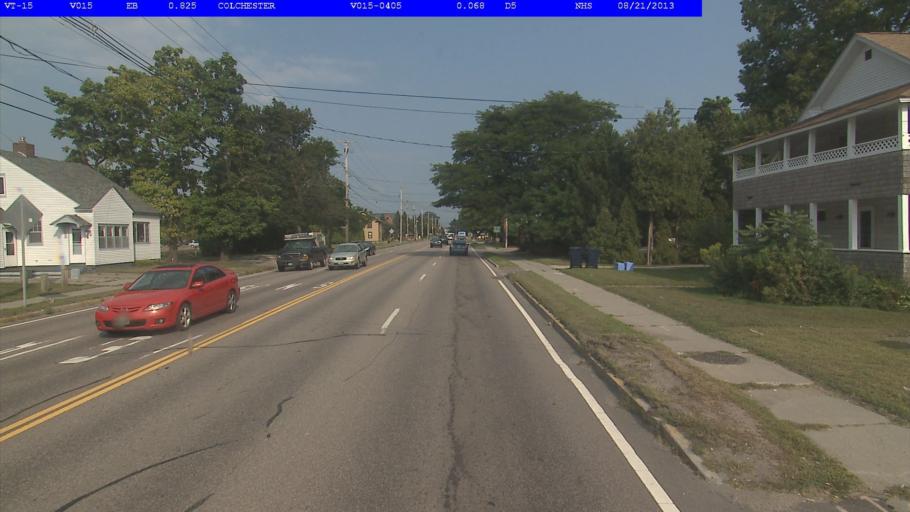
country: US
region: Vermont
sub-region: Chittenden County
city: Winooski
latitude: 44.4932
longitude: -73.1702
